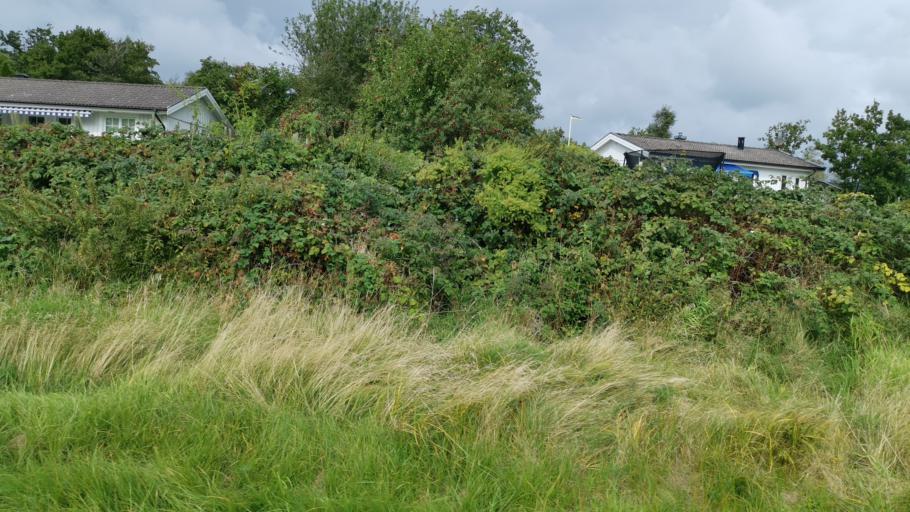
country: SE
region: Vaestra Goetaland
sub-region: Tjorns Kommun
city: Skaerhamn
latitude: 58.0537
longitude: 11.5830
